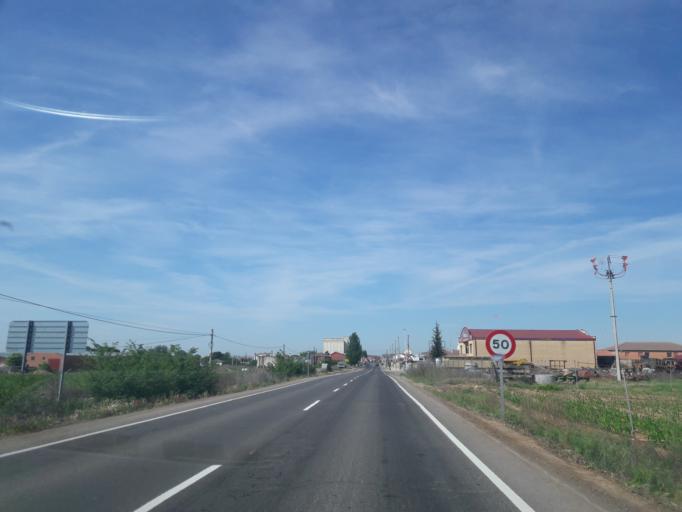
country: ES
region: Castille and Leon
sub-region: Provincia de Salamanca
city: Babilafuente
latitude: 40.9779
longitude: -5.4205
